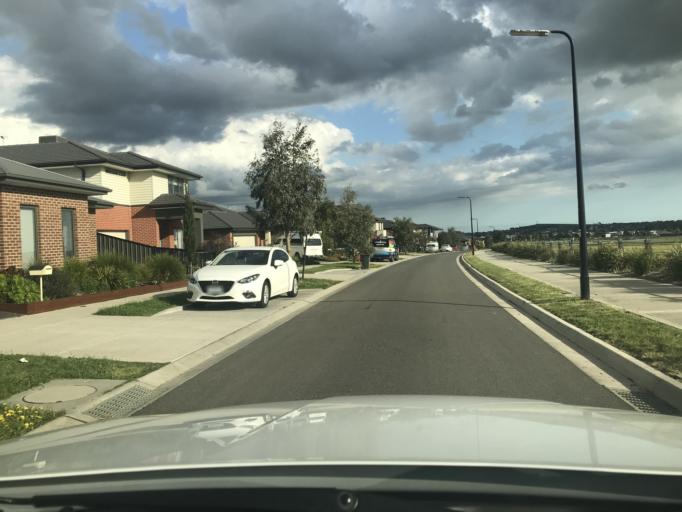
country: AU
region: Victoria
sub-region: Hume
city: Craigieburn
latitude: -37.5777
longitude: 144.9020
